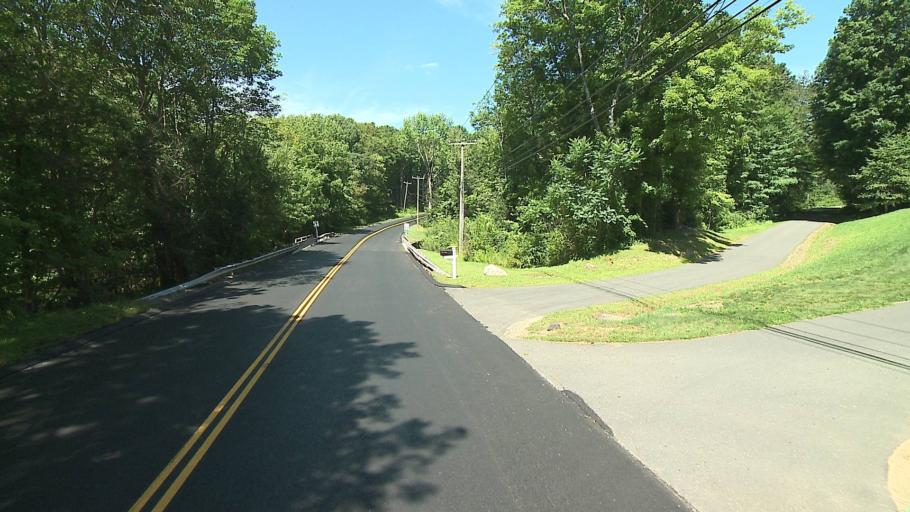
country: US
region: Connecticut
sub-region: Hartford County
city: West Simsbury
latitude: 41.9094
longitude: -72.8987
